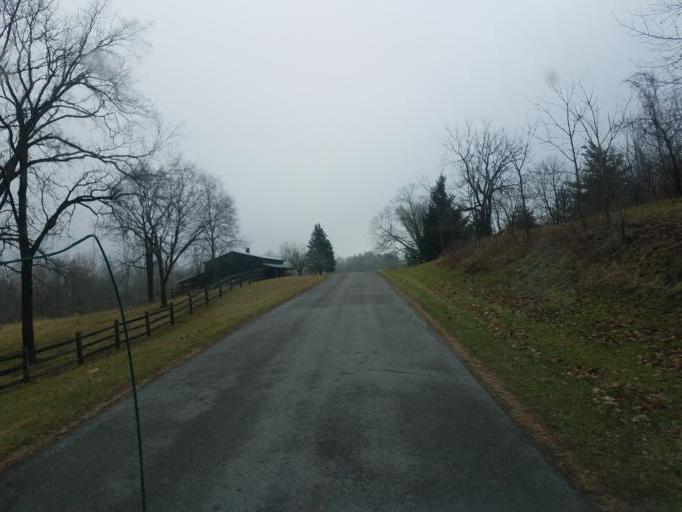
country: US
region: Ohio
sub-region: Champaign County
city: North Lewisburg
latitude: 40.2838
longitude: -83.6001
